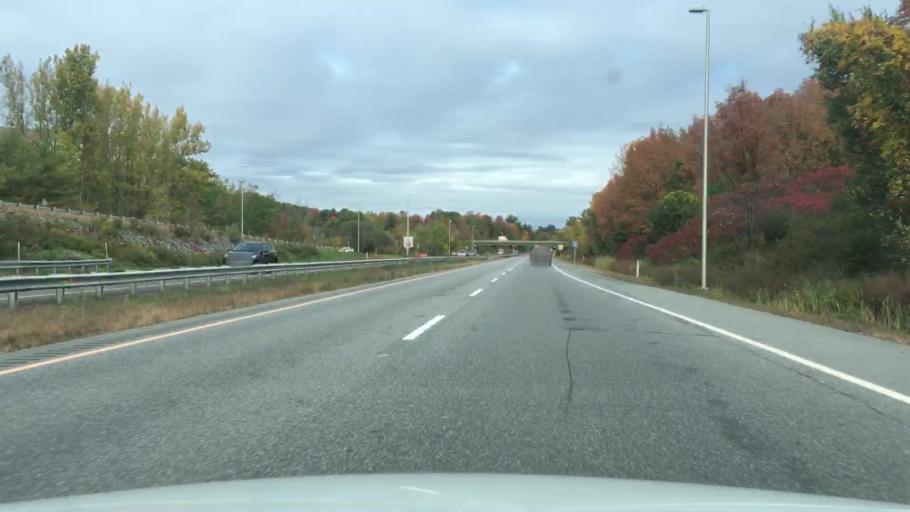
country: US
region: Maine
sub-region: Kennebec County
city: Augusta
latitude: 44.3169
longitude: -69.8118
